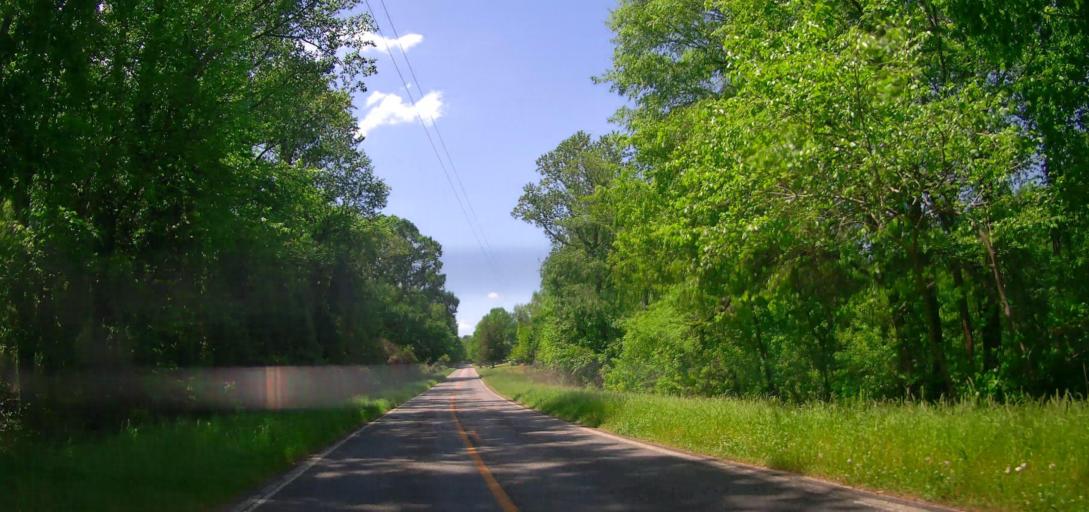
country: US
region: Georgia
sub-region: Jasper County
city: Monticello
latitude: 33.3134
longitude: -83.6697
